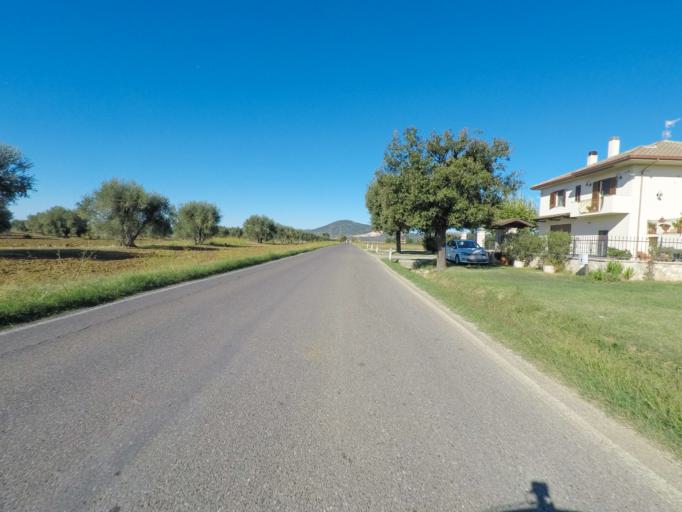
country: IT
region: Tuscany
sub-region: Provincia di Grosseto
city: Grosseto
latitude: 42.7705
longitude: 11.1391
